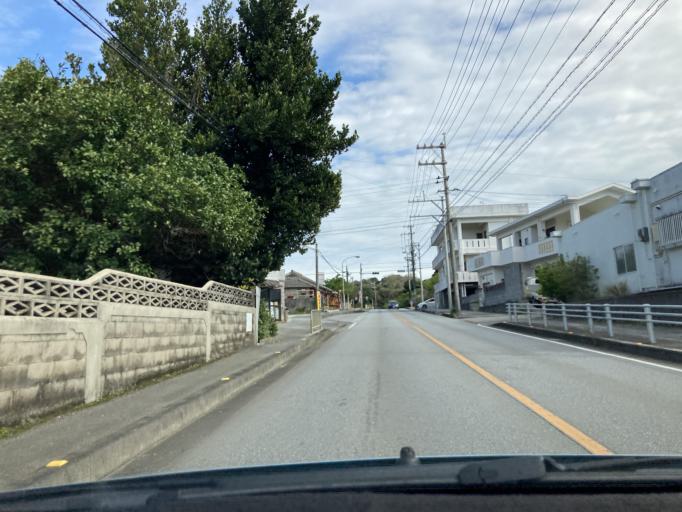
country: JP
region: Okinawa
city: Nago
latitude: 26.6969
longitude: 127.9423
